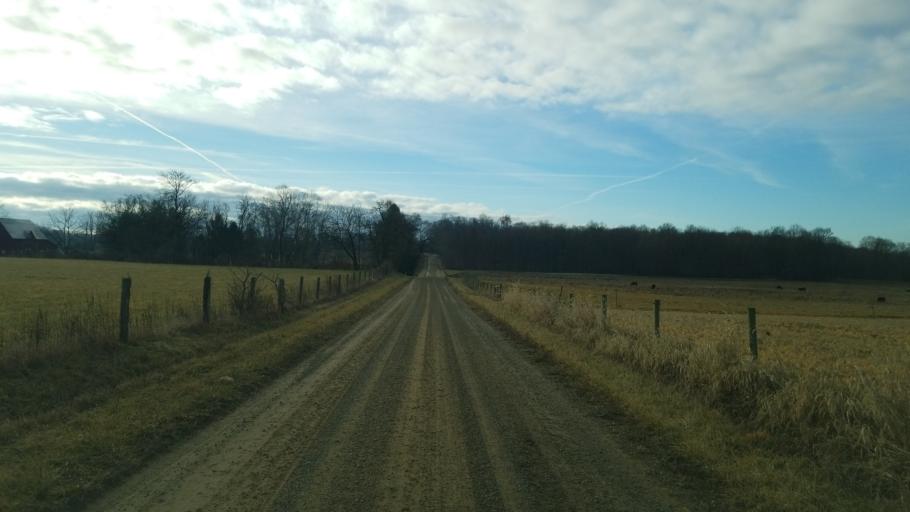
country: US
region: Ohio
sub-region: Knox County
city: Gambier
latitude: 40.3185
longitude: -82.3211
